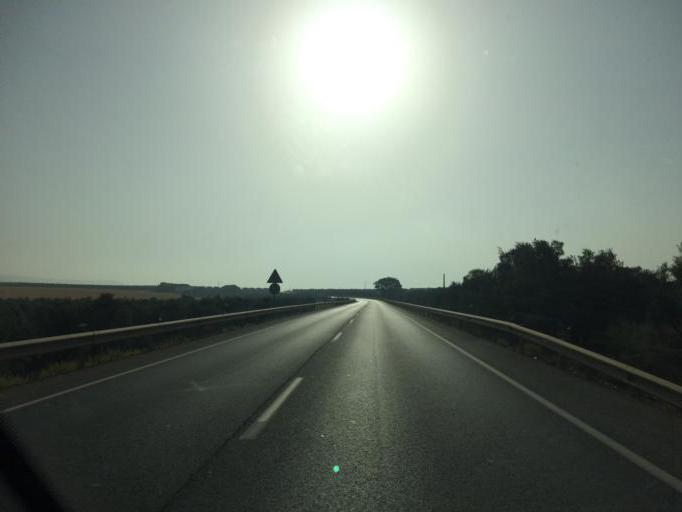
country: ES
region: Andalusia
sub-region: Provincia de Malaga
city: Humilladero
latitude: 37.0551
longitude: -4.7442
